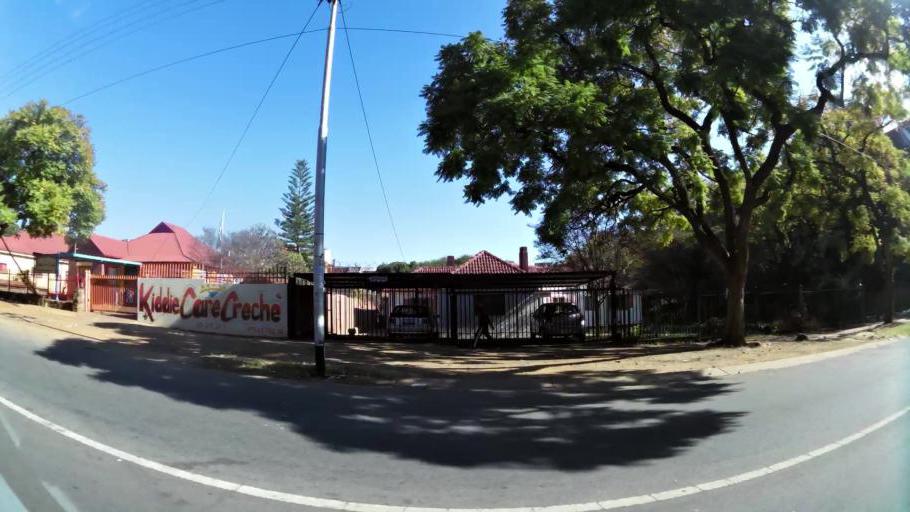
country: ZA
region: Gauteng
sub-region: City of Tshwane Metropolitan Municipality
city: Pretoria
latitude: -25.7563
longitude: 28.2065
